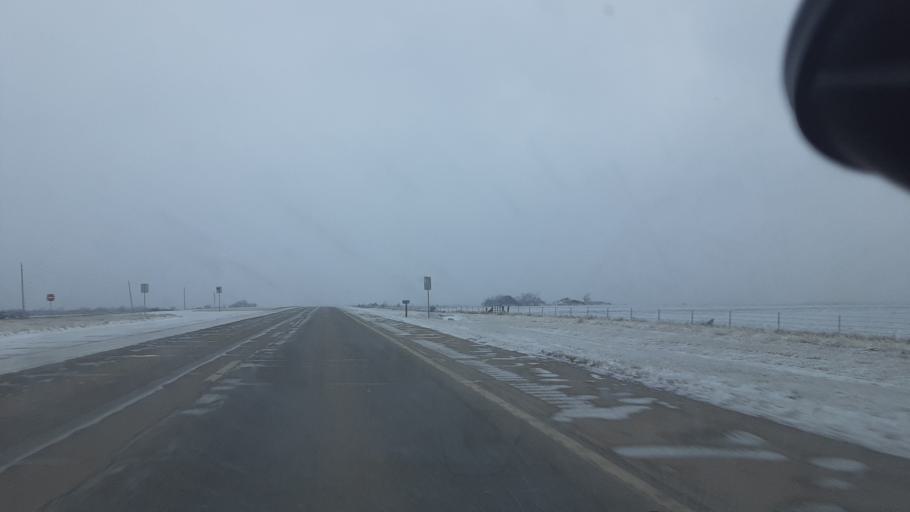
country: US
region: Oklahoma
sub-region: Logan County
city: Langston
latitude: 35.9235
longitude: -97.3229
